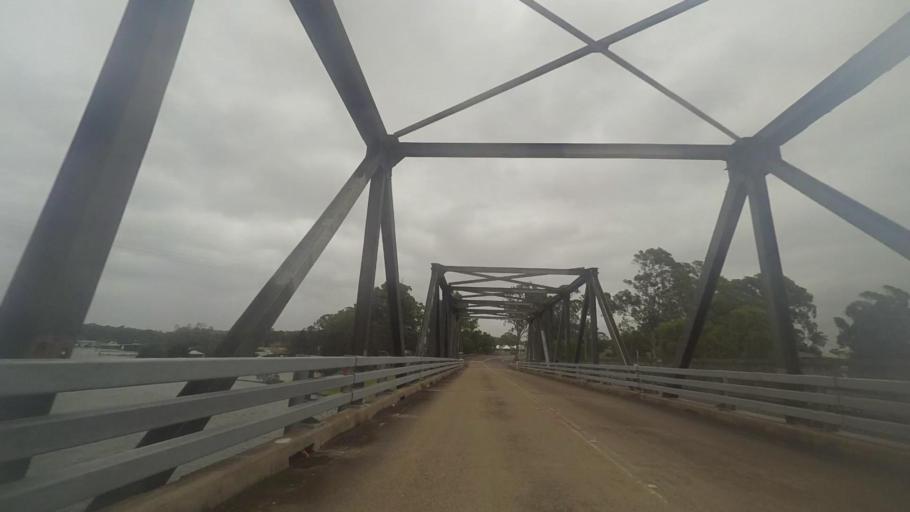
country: AU
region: New South Wales
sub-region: Port Stephens Shire
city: Port Stephens
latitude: -32.6543
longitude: 151.9687
